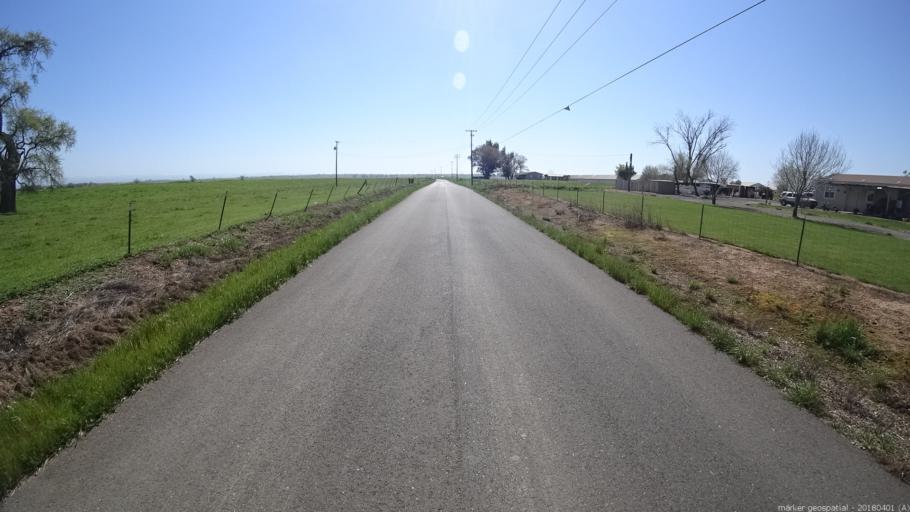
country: US
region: California
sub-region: Sacramento County
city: Rancho Murieta
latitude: 38.4692
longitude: -121.1621
